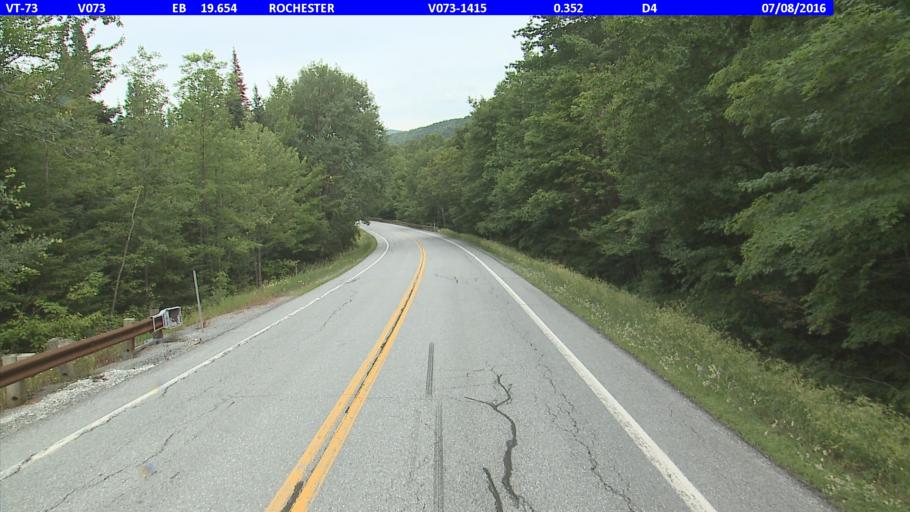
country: US
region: Vermont
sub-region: Rutland County
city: Brandon
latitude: 43.8408
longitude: -72.9574
